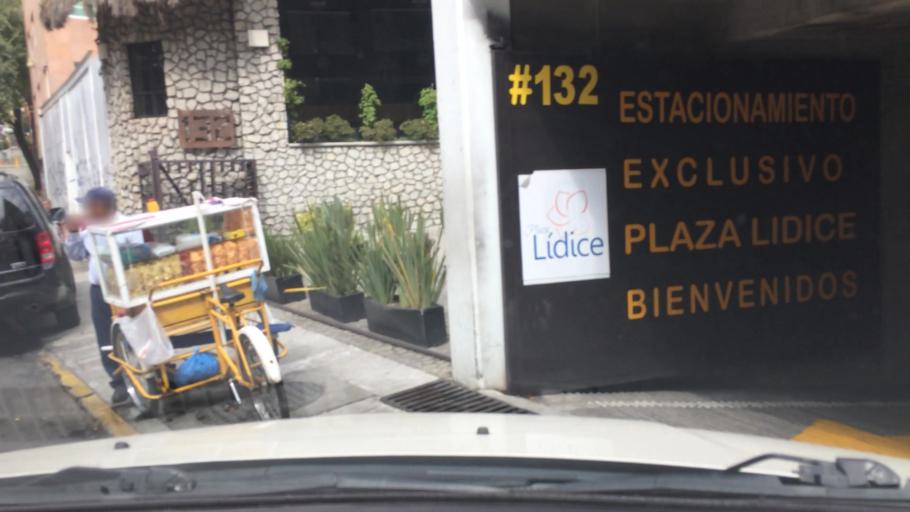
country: MX
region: Mexico City
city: Magdalena Contreras
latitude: 19.3233
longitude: -99.2232
